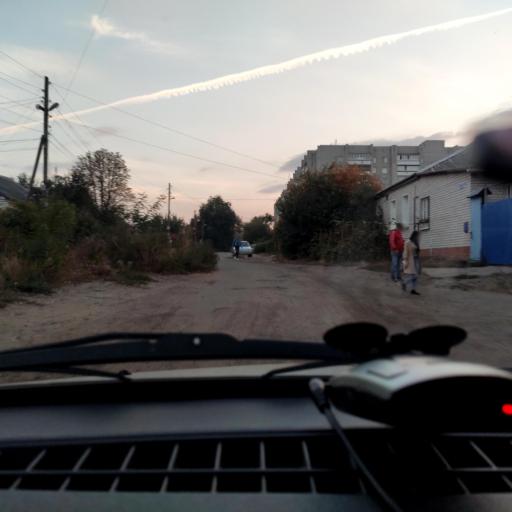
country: RU
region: Voronezj
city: Voronezh
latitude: 51.6755
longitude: 39.1602
